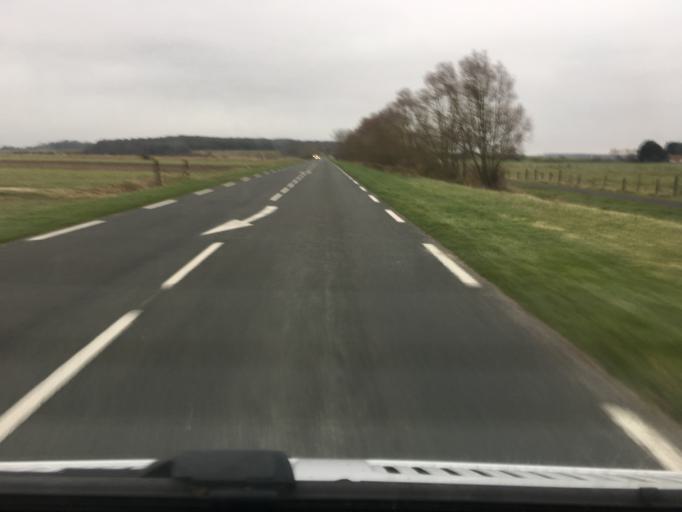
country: FR
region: Picardie
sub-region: Departement de la Somme
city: Pende
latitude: 50.1850
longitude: 1.5827
